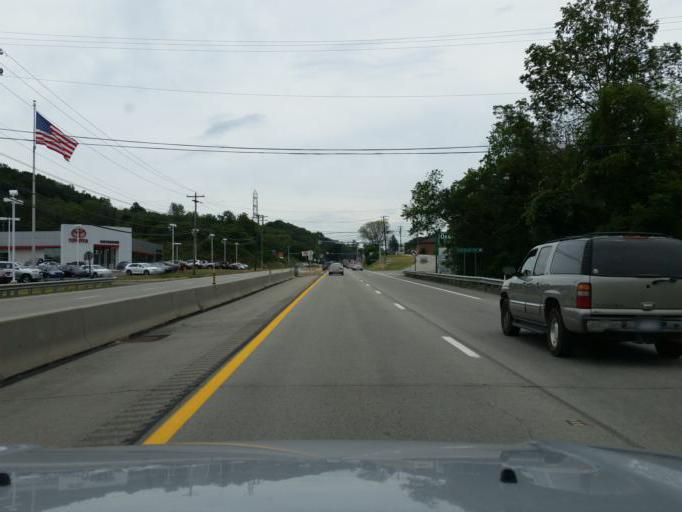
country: US
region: Pennsylvania
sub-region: Westmoreland County
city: Greensburg
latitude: 40.2982
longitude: -79.4827
